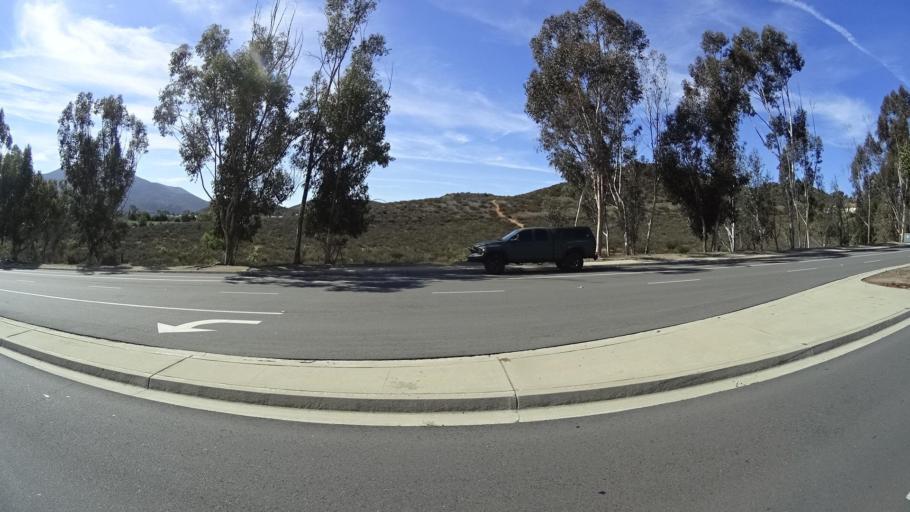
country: US
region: California
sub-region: San Diego County
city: Rancho San Diego
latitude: 32.7501
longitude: -116.9406
